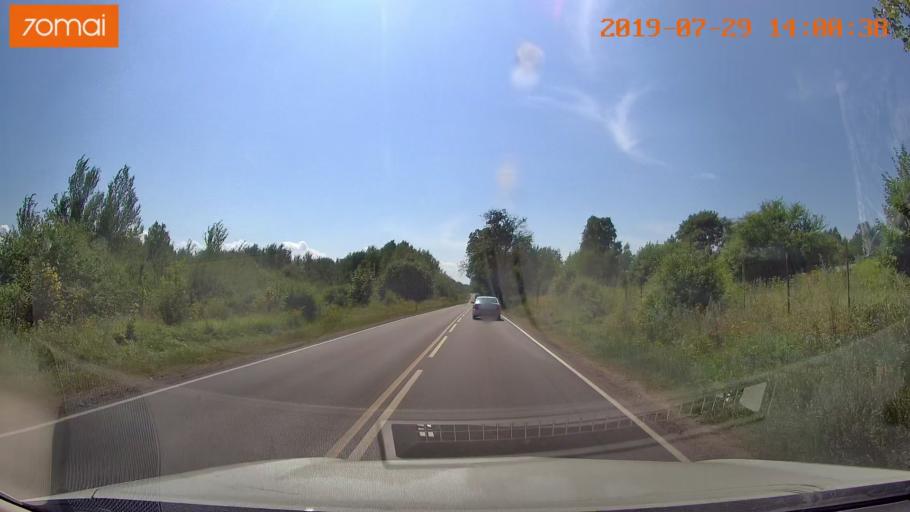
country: RU
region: Kaliningrad
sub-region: Gorod Kaliningrad
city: Baltiysk
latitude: 54.6768
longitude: 19.9268
